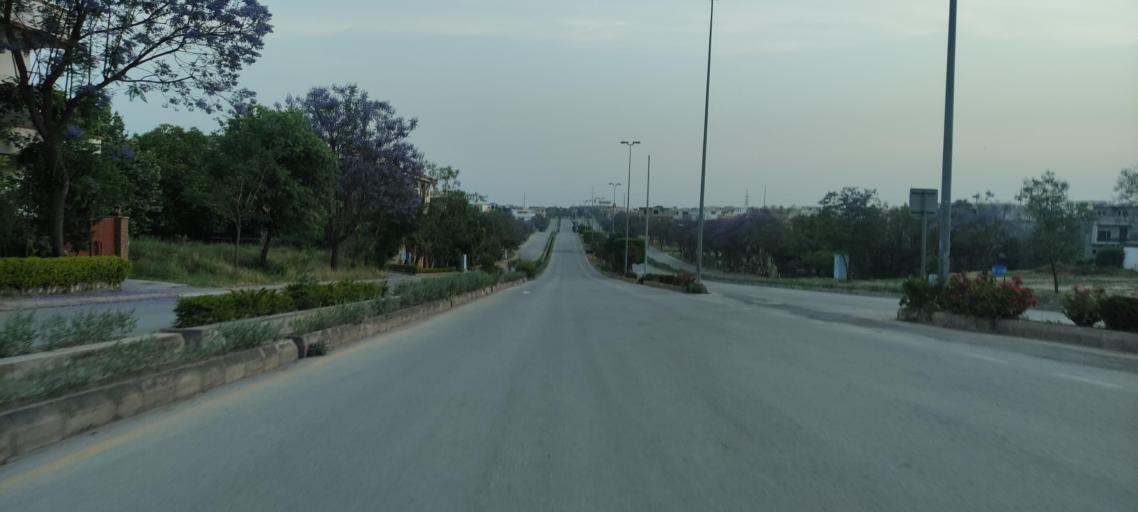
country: PK
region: Punjab
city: Rawalpindi
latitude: 33.5226
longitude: 73.1652
